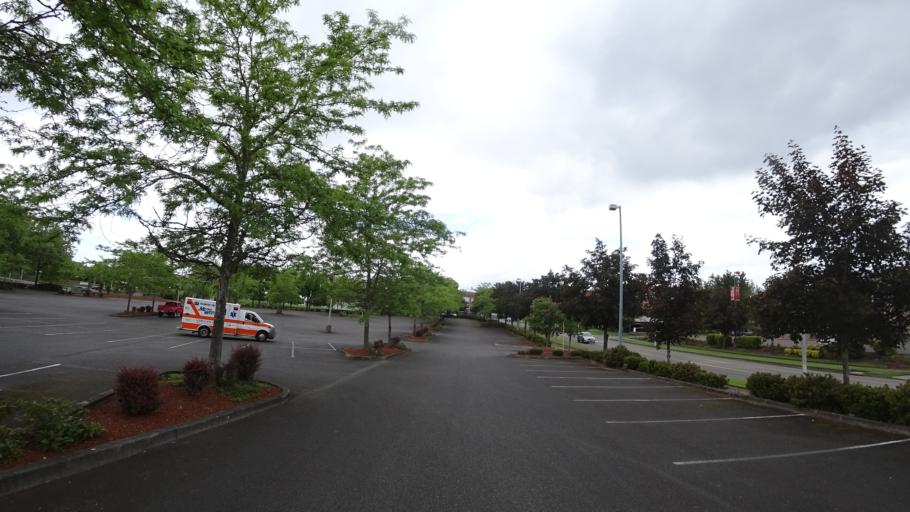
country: US
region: Oregon
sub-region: Washington County
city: Rockcreek
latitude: 45.5402
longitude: -122.8724
